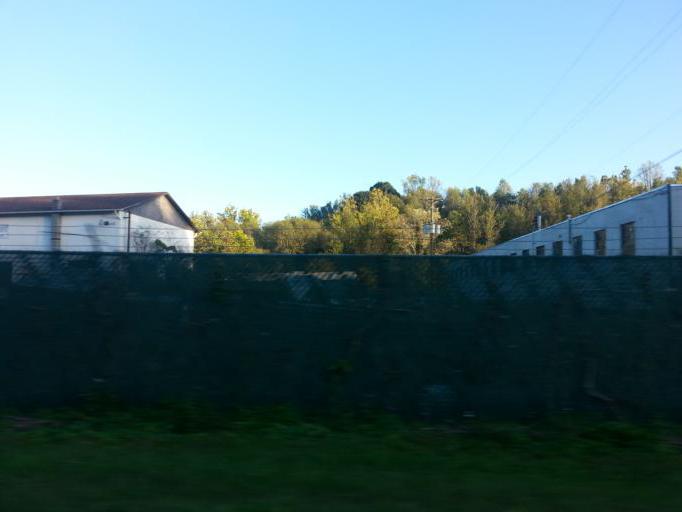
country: US
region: Tennessee
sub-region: Knox County
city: Knoxville
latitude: 35.9179
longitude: -83.9309
